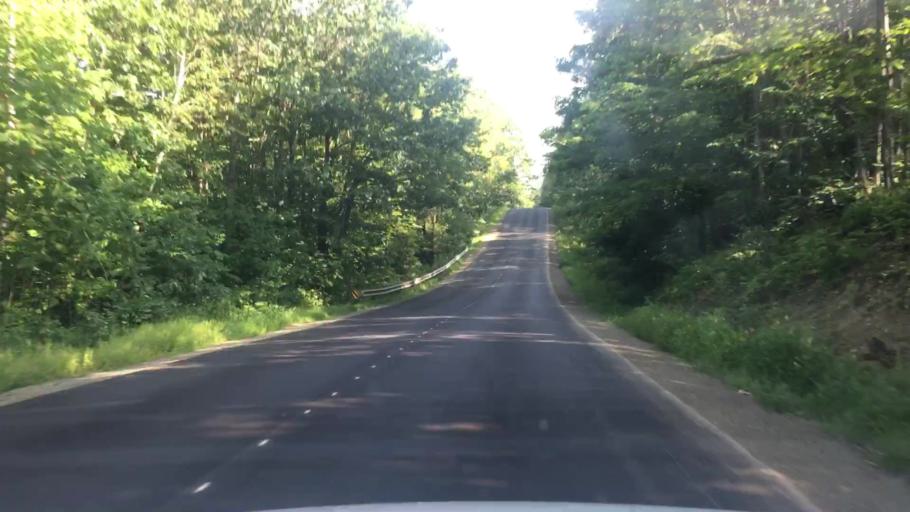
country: US
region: Maine
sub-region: Kennebec County
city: Waterville
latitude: 44.5750
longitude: -69.6589
